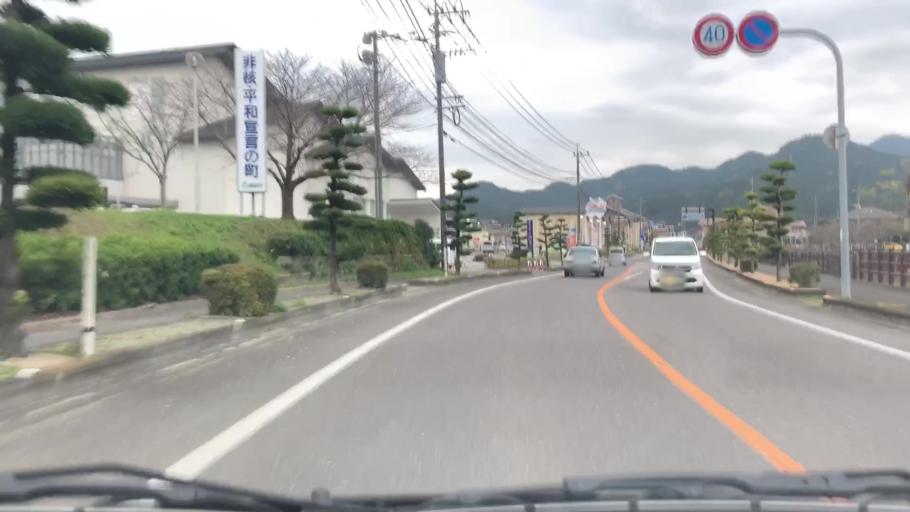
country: JP
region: Saga Prefecture
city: Kashima
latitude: 33.1309
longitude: 130.0615
